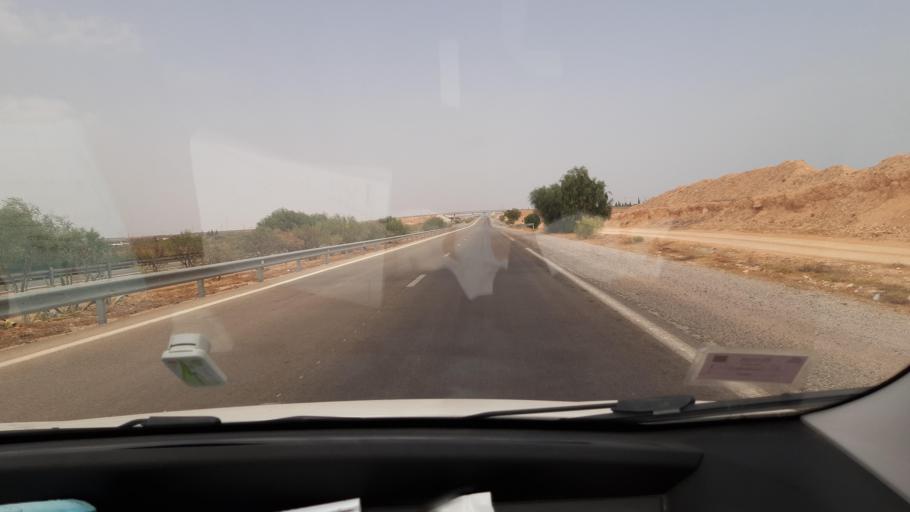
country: TN
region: Safaqis
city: Sfax
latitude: 34.8793
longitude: 10.7023
